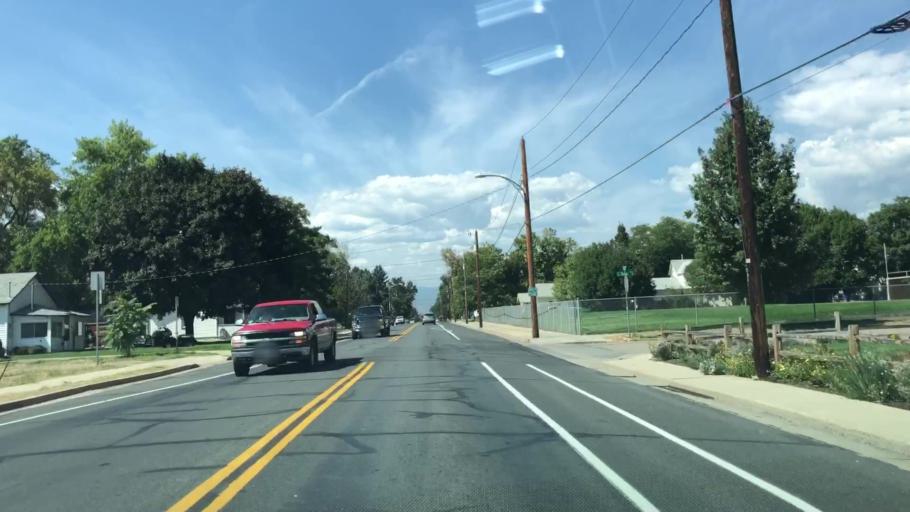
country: US
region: Colorado
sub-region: Larimer County
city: Loveland
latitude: 40.3928
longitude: -105.0789
